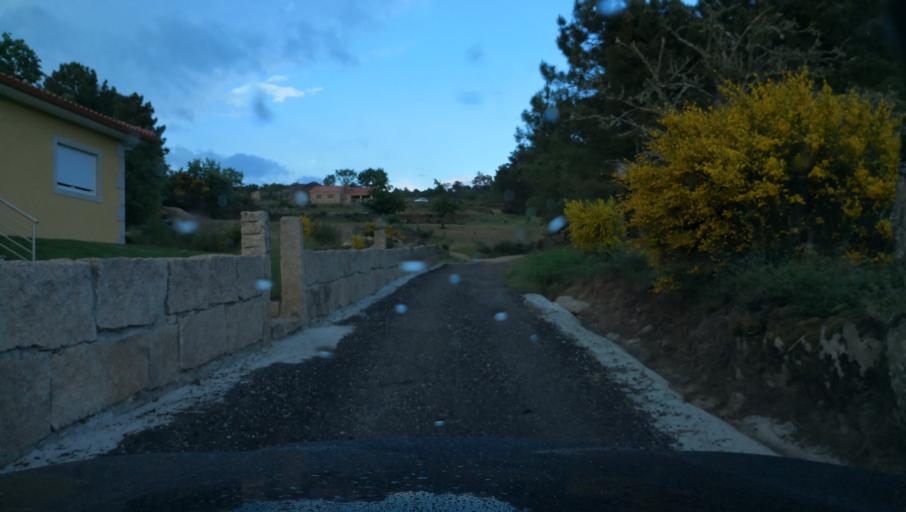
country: PT
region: Vila Real
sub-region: Vila Real
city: Vila Real
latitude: 41.3144
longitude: -7.6804
